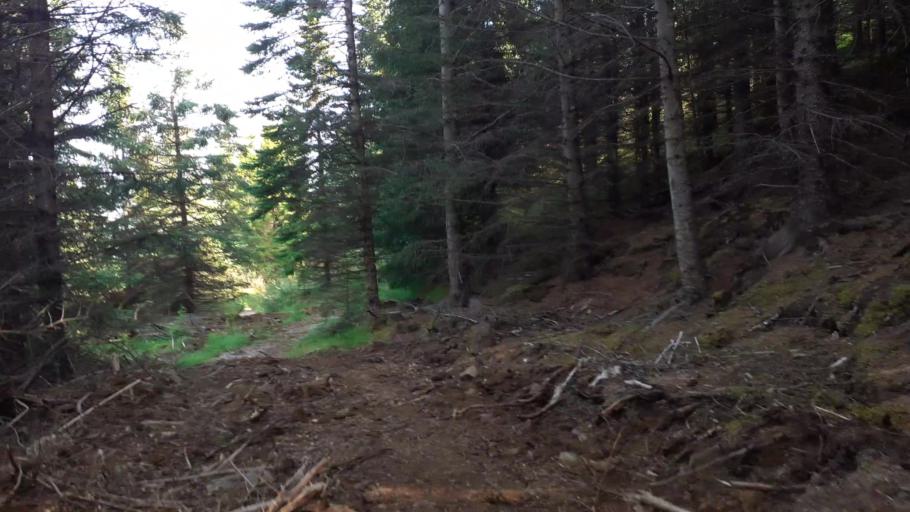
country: IS
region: West
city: Borgarnes
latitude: 64.6588
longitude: -21.7106
